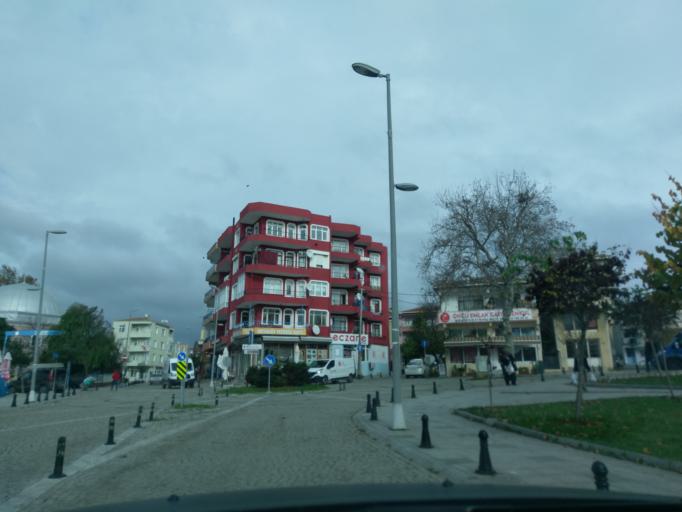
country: TR
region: Istanbul
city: Ortakoy
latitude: 41.0997
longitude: 28.3762
